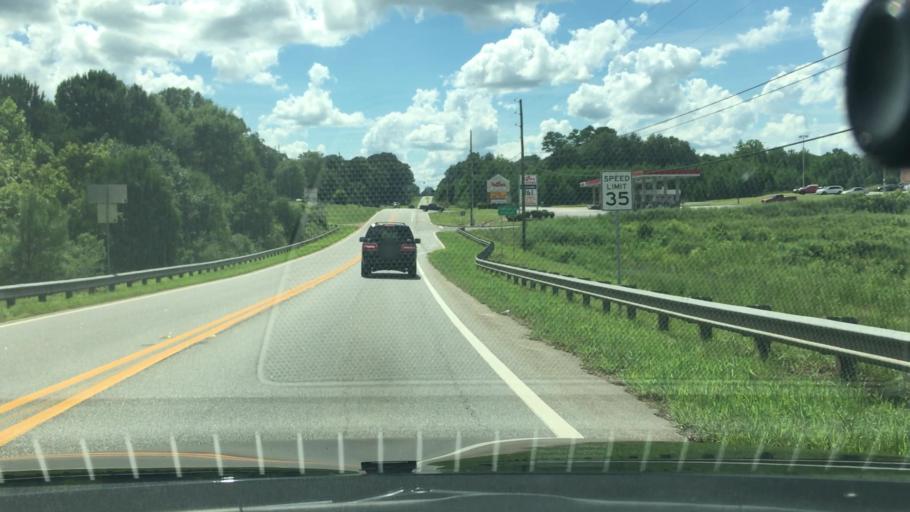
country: US
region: Georgia
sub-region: Putnam County
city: Eatonton
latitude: 33.3195
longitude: -83.4095
